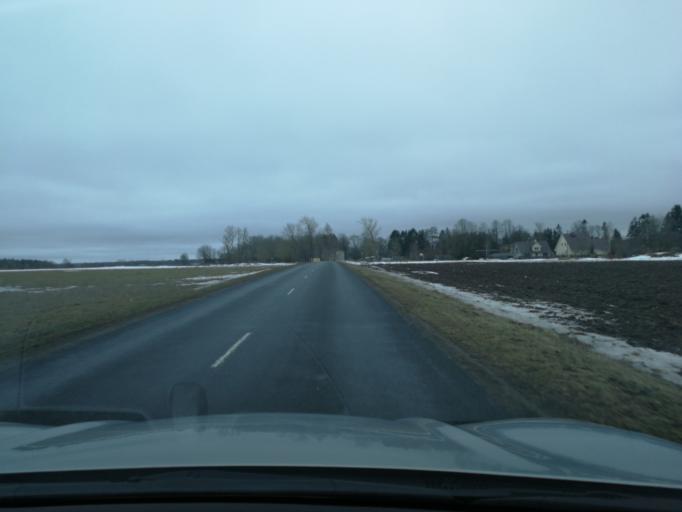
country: EE
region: Harju
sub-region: Kiili vald
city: Kiili
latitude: 59.2775
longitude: 24.8748
